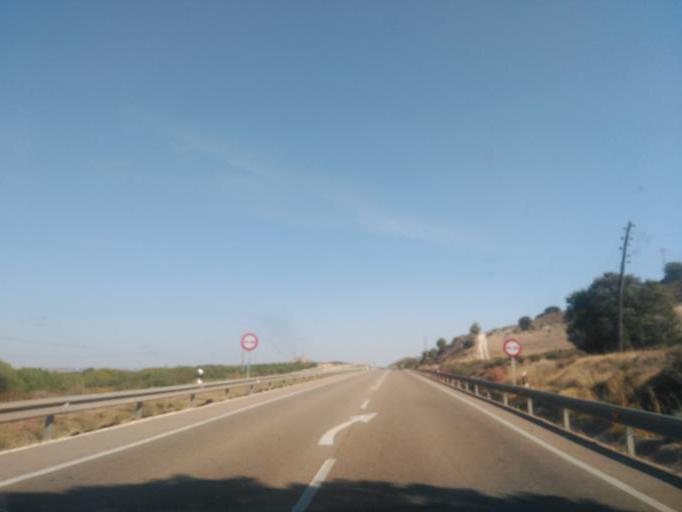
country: ES
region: Castille and Leon
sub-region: Provincia de Valladolid
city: Valbuena de Duero
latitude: 41.6250
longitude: -4.2744
